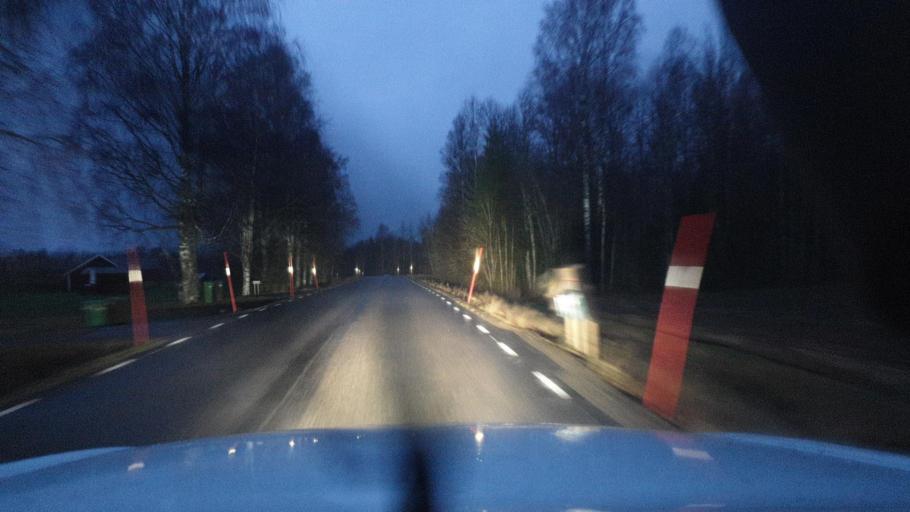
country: SE
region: Vaermland
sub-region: Torsby Kommun
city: Torsby
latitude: 59.9851
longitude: 12.8678
